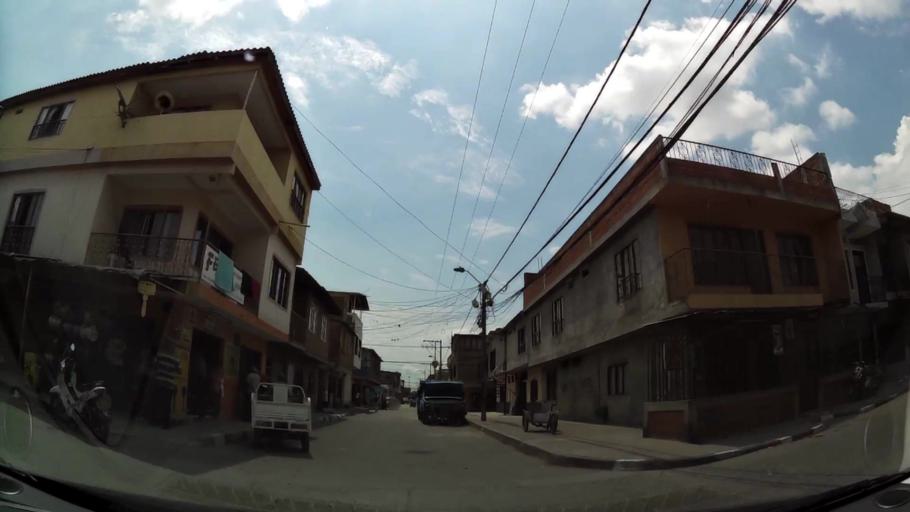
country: CO
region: Valle del Cauca
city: Cali
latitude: 3.4756
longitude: -76.4806
